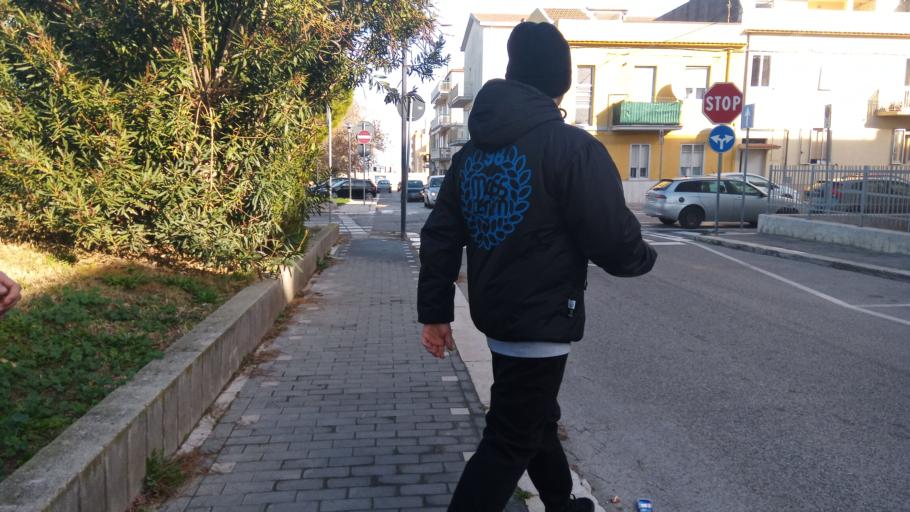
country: IT
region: Molise
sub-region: Provincia di Campobasso
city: Termoli
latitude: 42.0018
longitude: 14.9881
